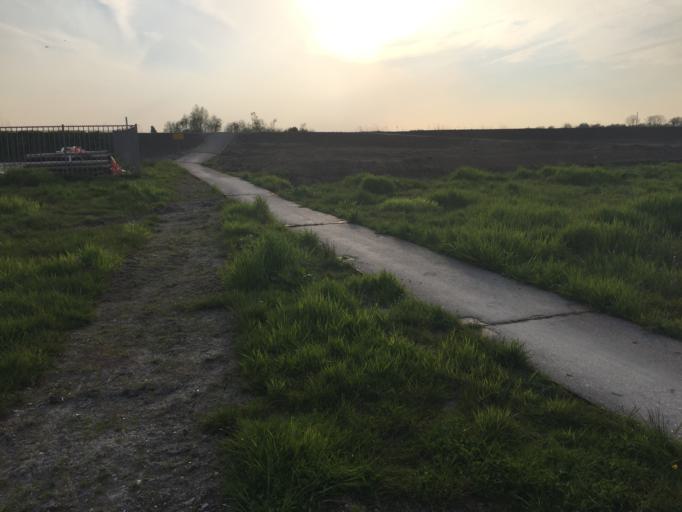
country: NL
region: Utrecht
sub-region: Gemeente Woerden
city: Woerden
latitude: 52.1413
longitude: 4.8721
